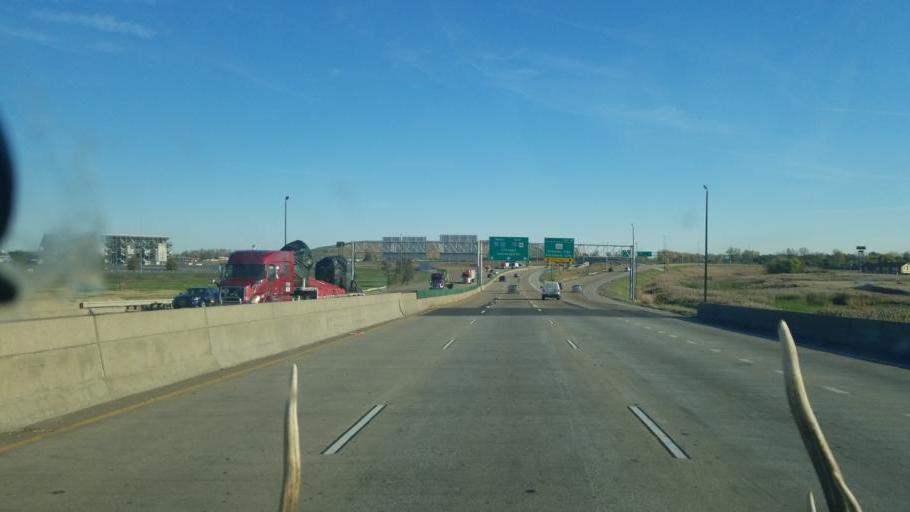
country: US
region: Illinois
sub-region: Saint Clair County
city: East Saint Louis
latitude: 38.6395
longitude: -90.1346
